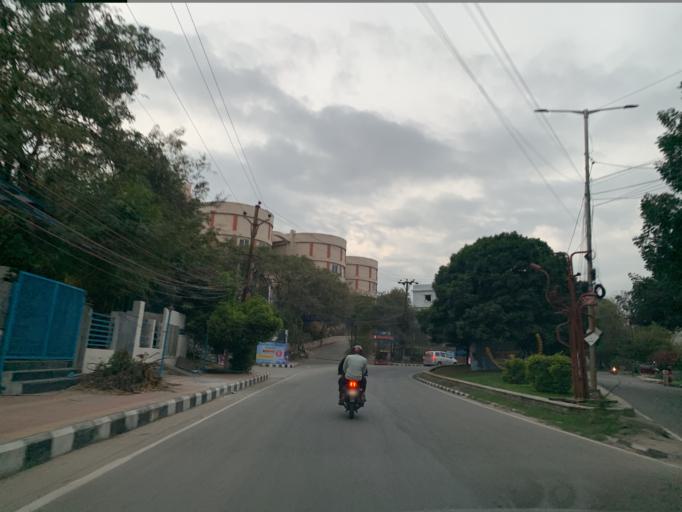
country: IN
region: Telangana
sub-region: Rangareddi
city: Kukatpalli
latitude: 17.4363
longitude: 78.3971
